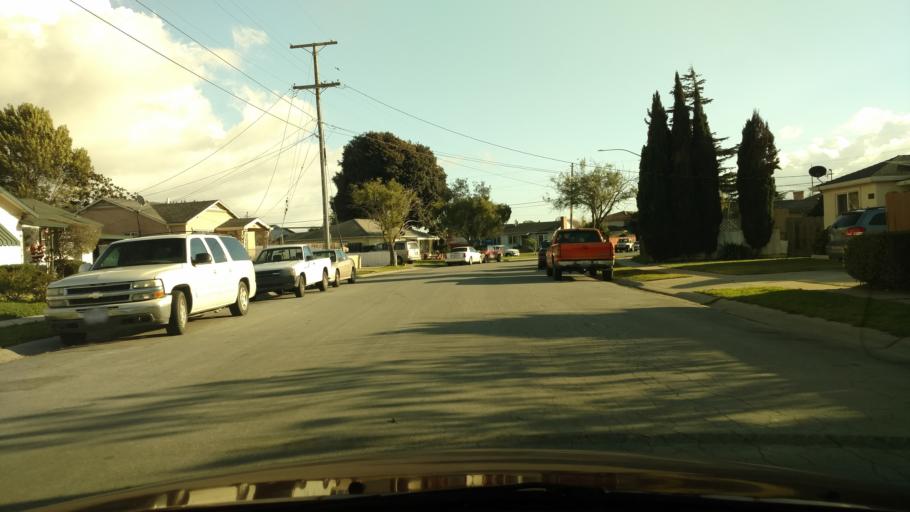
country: US
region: California
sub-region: Monterey County
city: Salinas
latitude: 36.6749
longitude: -121.6041
